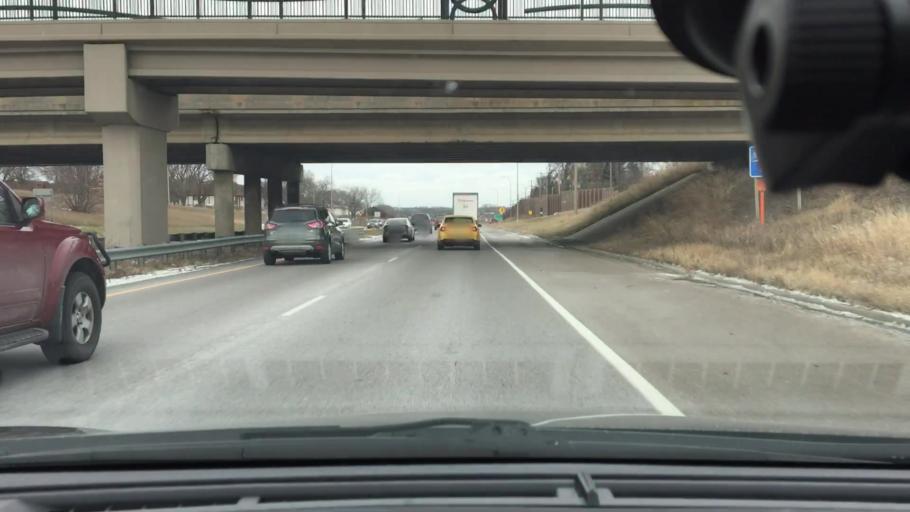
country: US
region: Minnesota
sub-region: Hennepin County
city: New Hope
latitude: 45.0218
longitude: -93.4006
